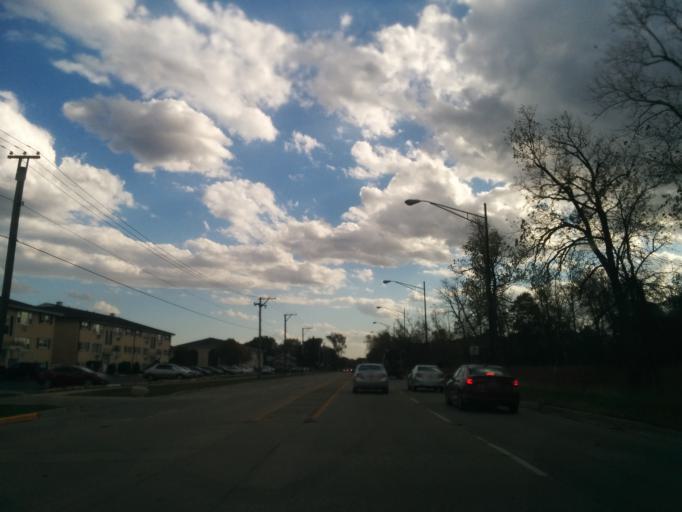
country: US
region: Illinois
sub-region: Cook County
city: Norridge
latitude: 41.9714
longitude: -87.8465
